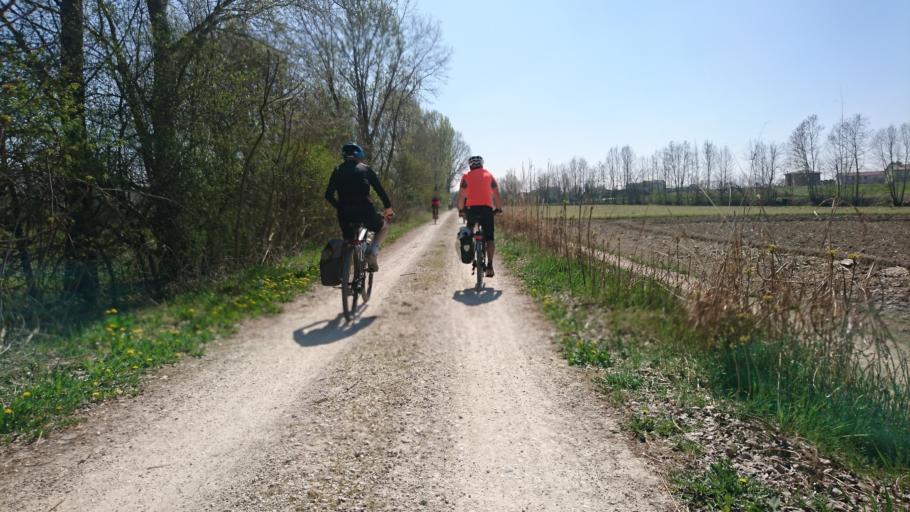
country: IT
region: Veneto
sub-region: Provincia di Padova
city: Piazzola sul Brenta
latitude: 45.5685
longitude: 11.7603
